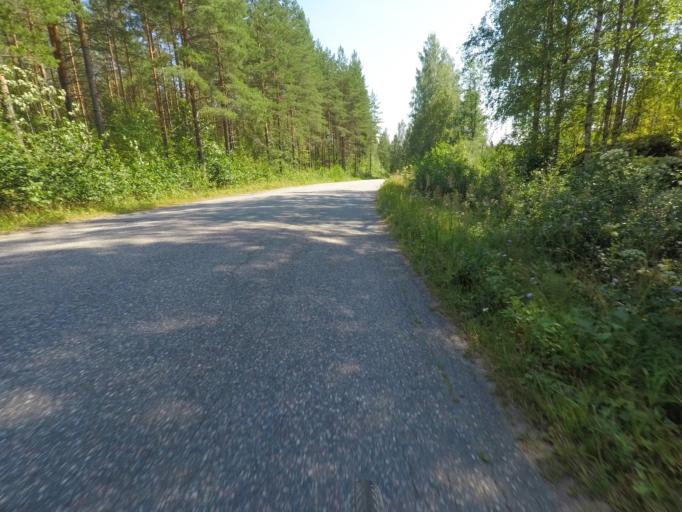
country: FI
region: Southern Savonia
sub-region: Mikkeli
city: Puumala
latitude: 61.4227
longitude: 28.1049
